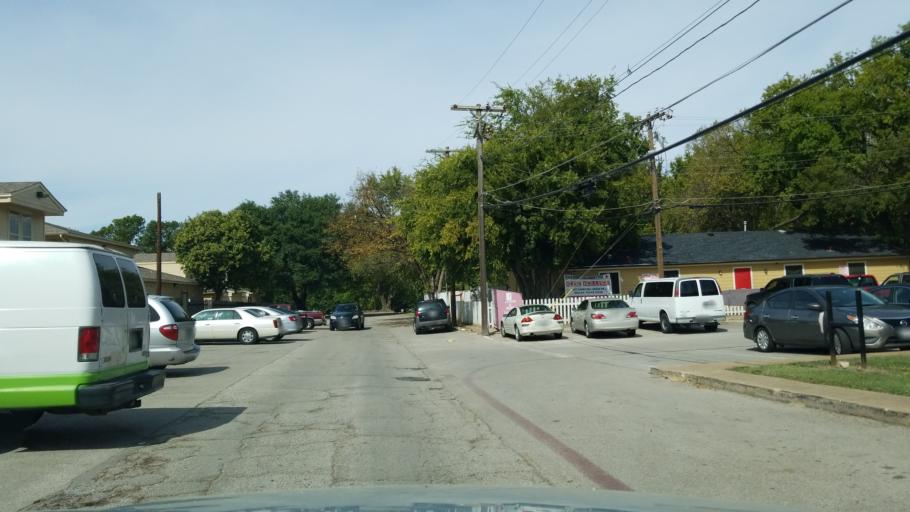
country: US
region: Texas
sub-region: Dallas County
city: Highland Park
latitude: 32.7976
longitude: -96.7223
